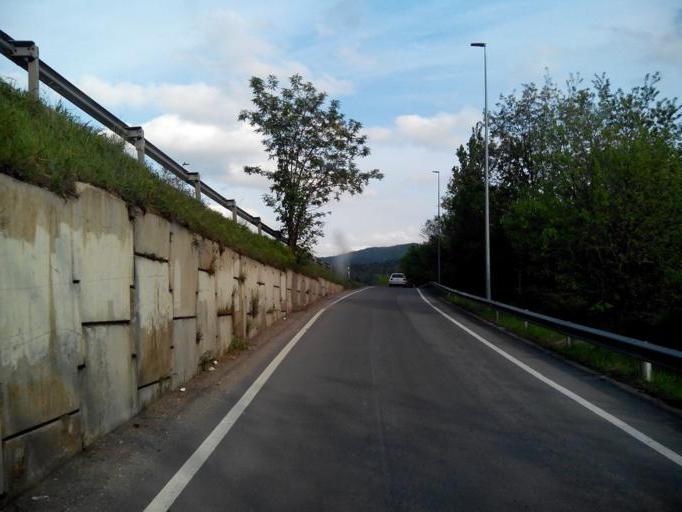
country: ES
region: Catalonia
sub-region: Provincia de Girona
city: MeteOlot
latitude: 42.1960
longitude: 2.5002
